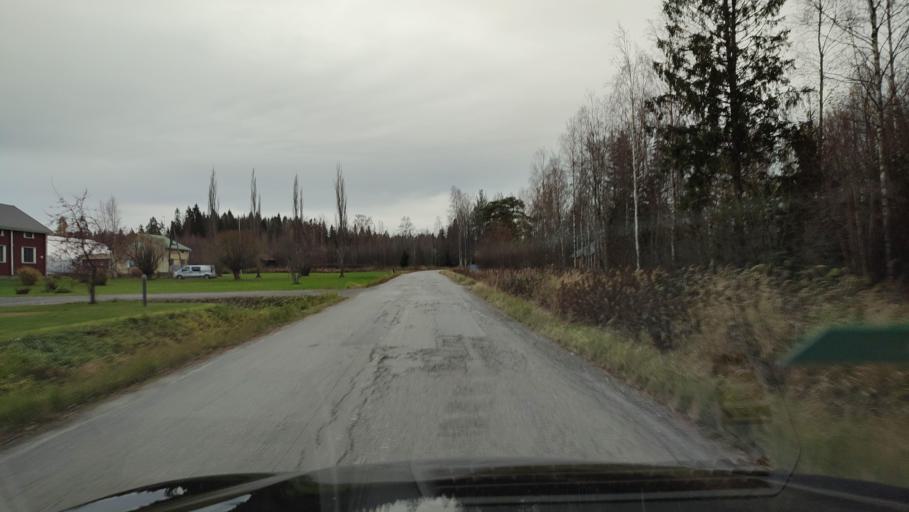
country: FI
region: Ostrobothnia
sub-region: Sydosterbotten
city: Naerpes
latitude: 62.4282
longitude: 21.4181
